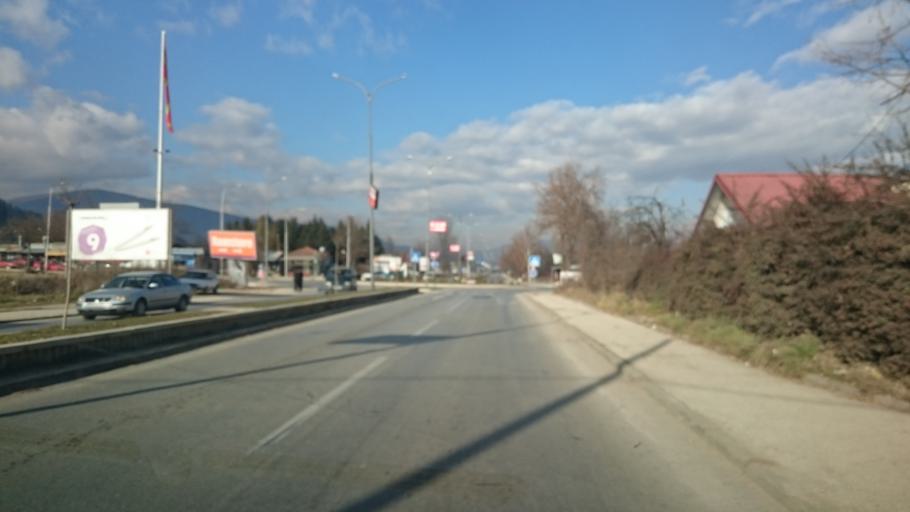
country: MK
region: Kicevo
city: Kicevo
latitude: 41.5119
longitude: 20.9524
